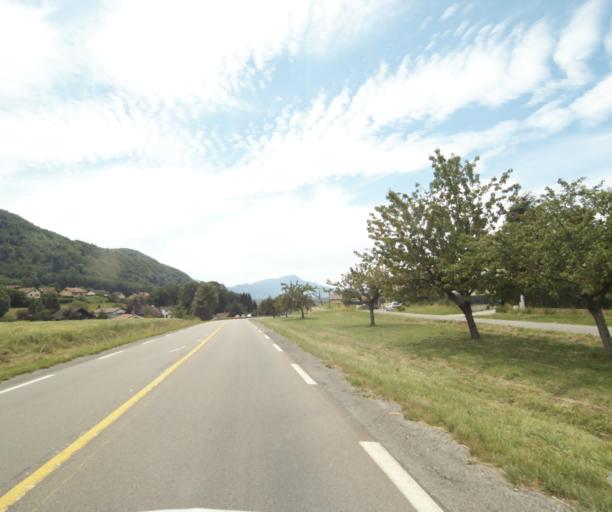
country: FR
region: Rhone-Alpes
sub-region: Departement de la Haute-Savoie
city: Allinges
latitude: 46.3328
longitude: 6.4501
